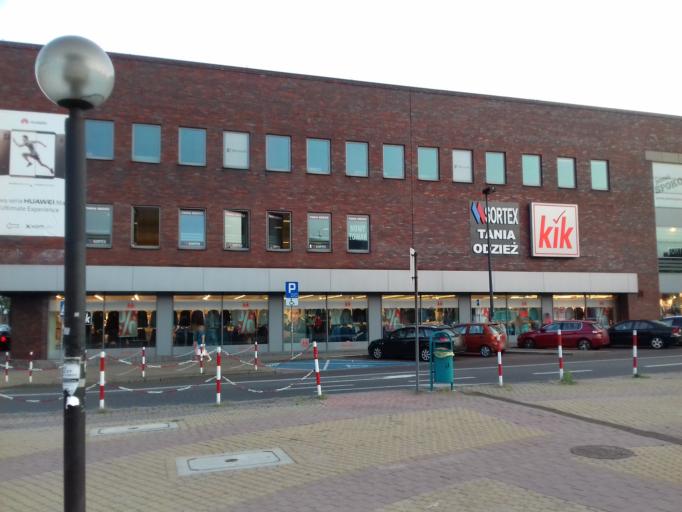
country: PL
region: Silesian Voivodeship
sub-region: Czestochowa
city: Czestochowa
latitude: 50.8086
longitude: 19.1192
